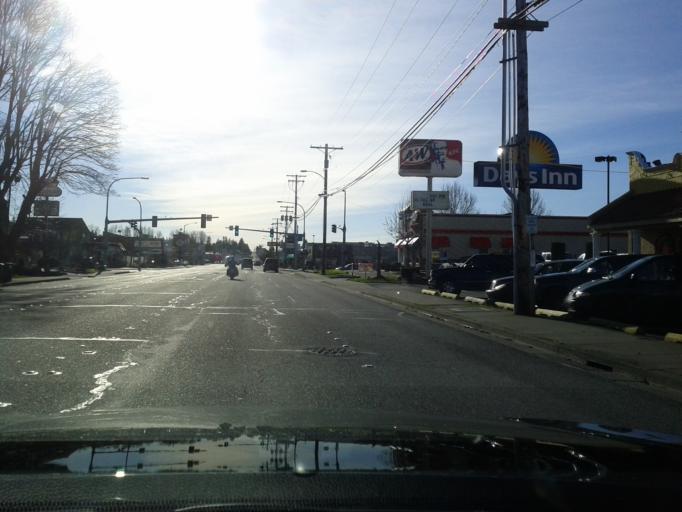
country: US
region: Washington
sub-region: Skagit County
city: Mount Vernon
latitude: 48.4389
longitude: -122.3352
